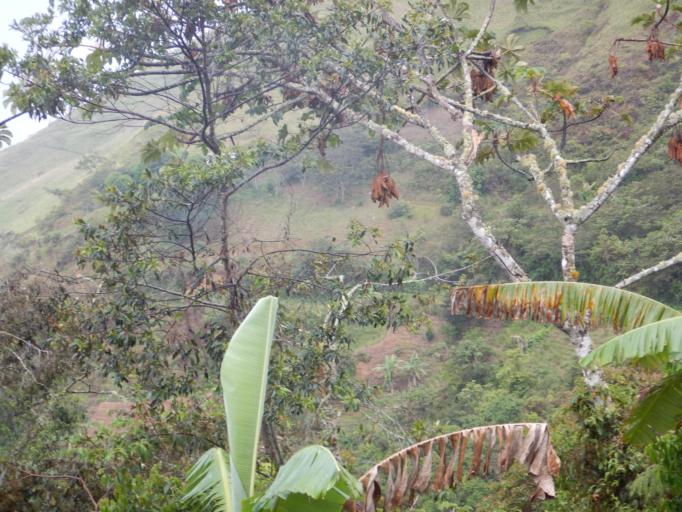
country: BO
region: La Paz
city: Coroico
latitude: -16.1396
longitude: -67.7468
